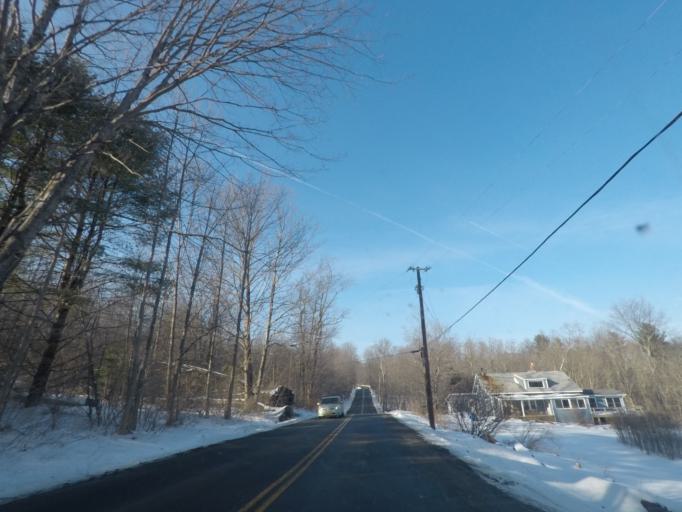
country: US
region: Massachusetts
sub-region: Berkshire County
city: Richmond
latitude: 42.5236
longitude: -73.3799
